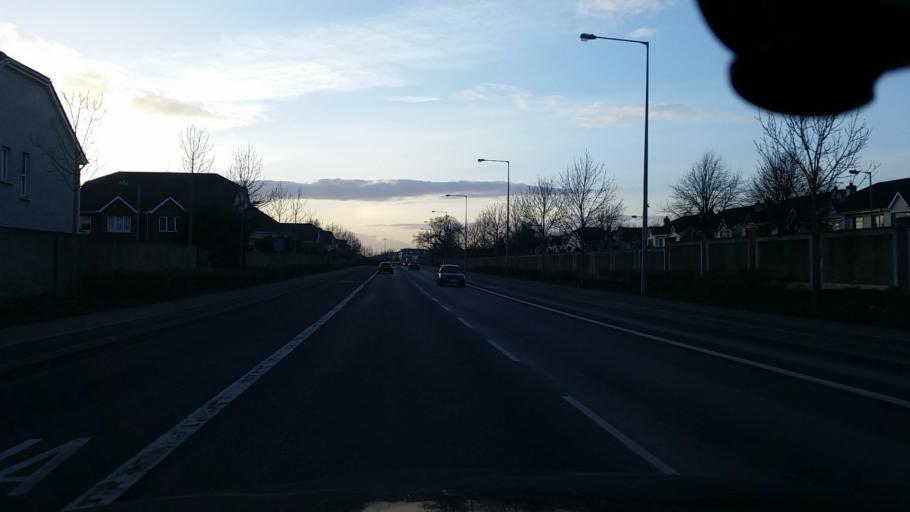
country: IE
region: Leinster
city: Hartstown
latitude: 53.3894
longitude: -6.4224
